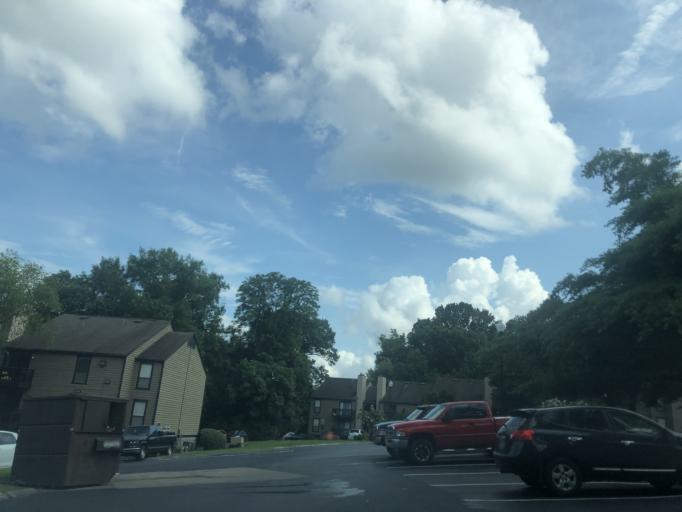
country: US
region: Tennessee
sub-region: Davidson County
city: Lakewood
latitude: 36.1624
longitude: -86.6317
